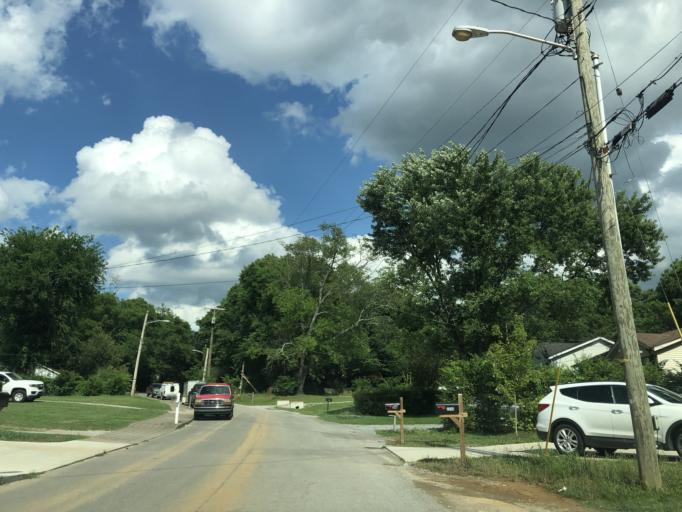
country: US
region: Tennessee
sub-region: Davidson County
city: Nashville
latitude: 36.2080
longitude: -86.7609
